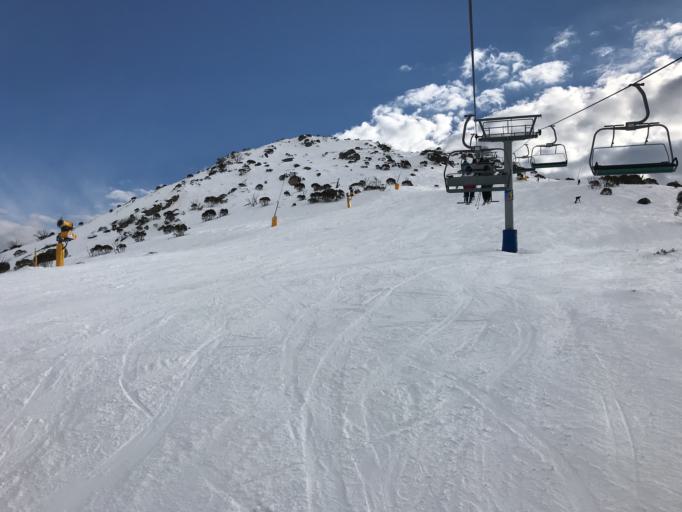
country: AU
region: New South Wales
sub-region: Snowy River
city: Jindabyne
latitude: -36.3782
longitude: 148.4023
